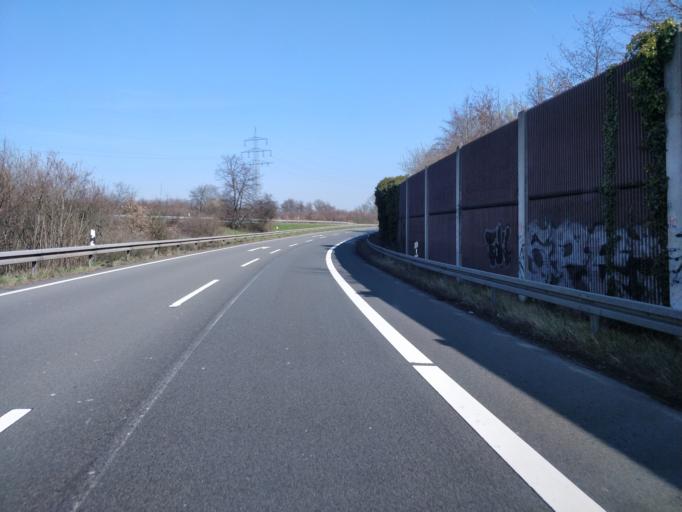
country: DE
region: North Rhine-Westphalia
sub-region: Regierungsbezirk Dusseldorf
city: Neuss
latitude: 51.1794
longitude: 6.7091
